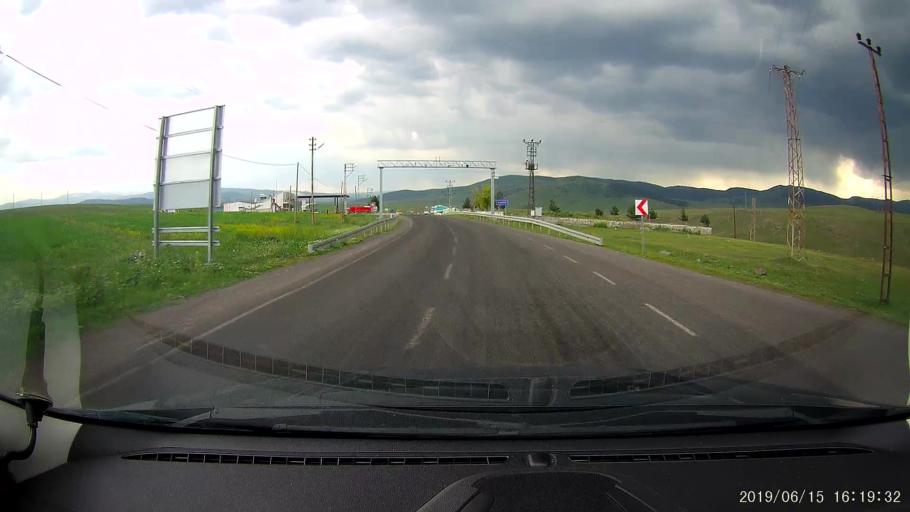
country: TR
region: Ardahan
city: Hanak
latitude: 41.2274
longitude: 42.8498
